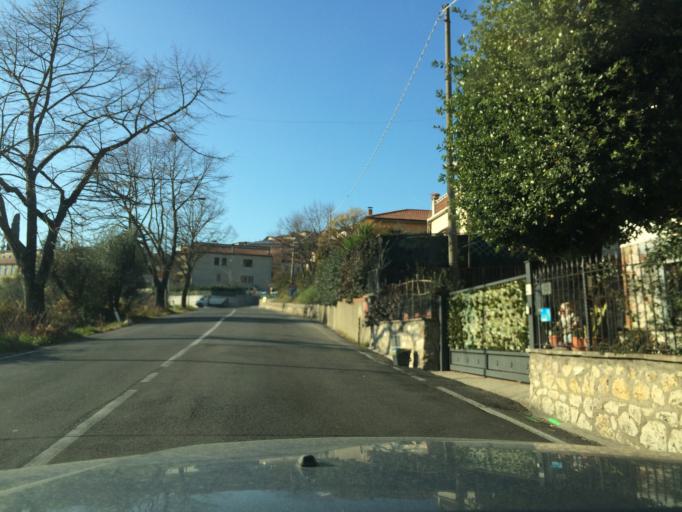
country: IT
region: Umbria
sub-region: Provincia di Terni
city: Fornole
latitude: 42.5431
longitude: 12.4596
